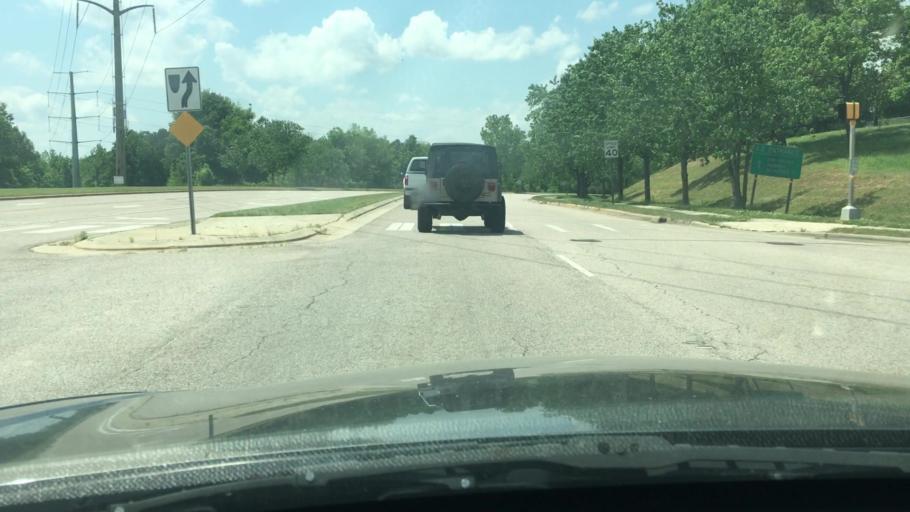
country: US
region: North Carolina
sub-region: Wake County
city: West Raleigh
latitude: 35.7613
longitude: -78.6633
